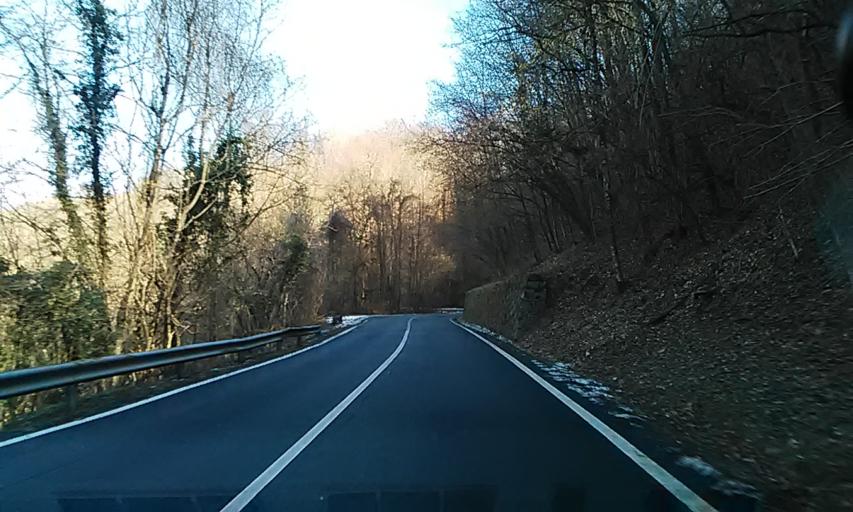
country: IT
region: Piedmont
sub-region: Provincia di Vercelli
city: Cellio
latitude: 45.7361
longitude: 8.3022
